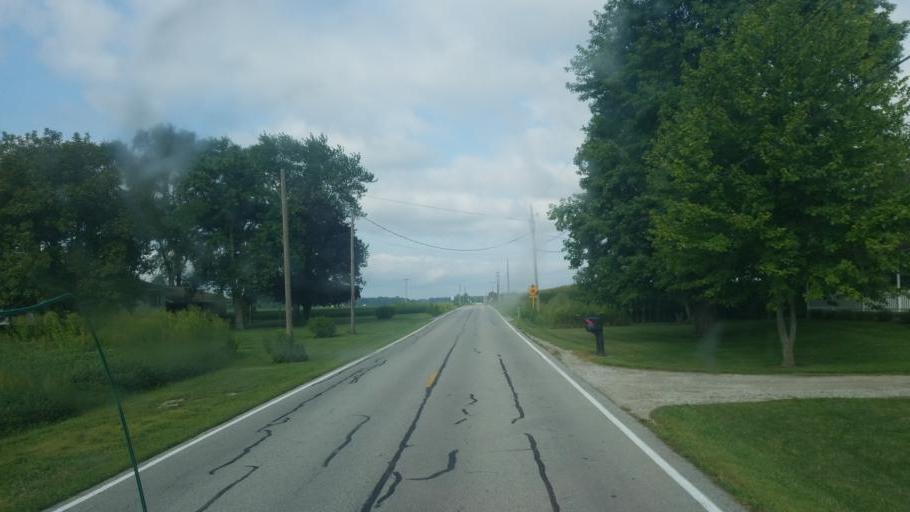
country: US
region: Ohio
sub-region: Marion County
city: Marion
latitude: 40.5641
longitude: -83.0426
